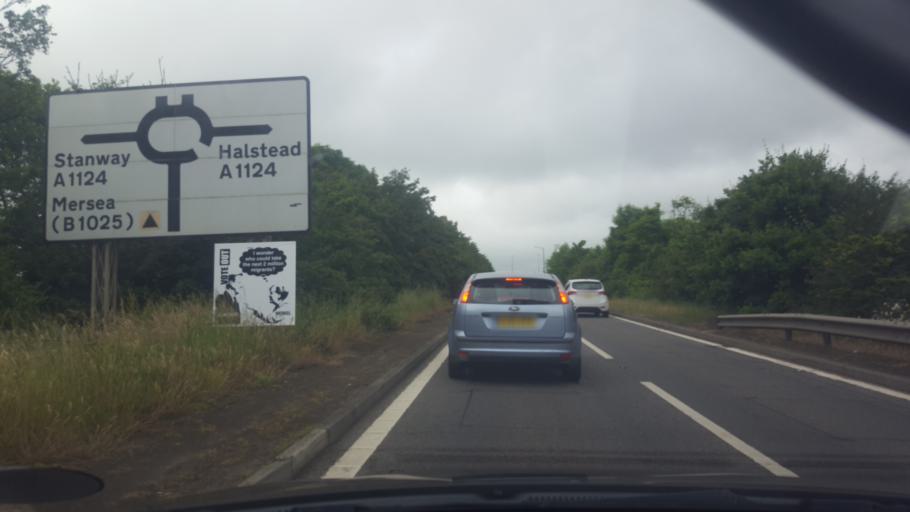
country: GB
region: England
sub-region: Essex
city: Eight Ash Green
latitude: 51.8903
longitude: 0.8311
